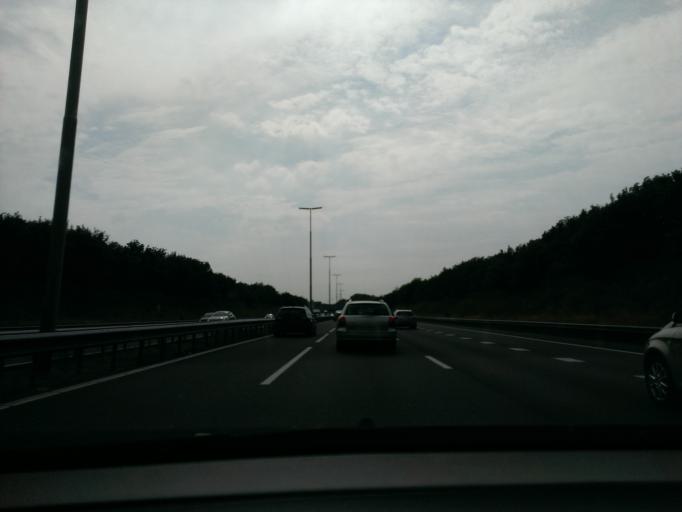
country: NL
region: Overijssel
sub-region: Gemeente Zwolle
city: Zwolle
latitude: 52.5249
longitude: 6.1080
